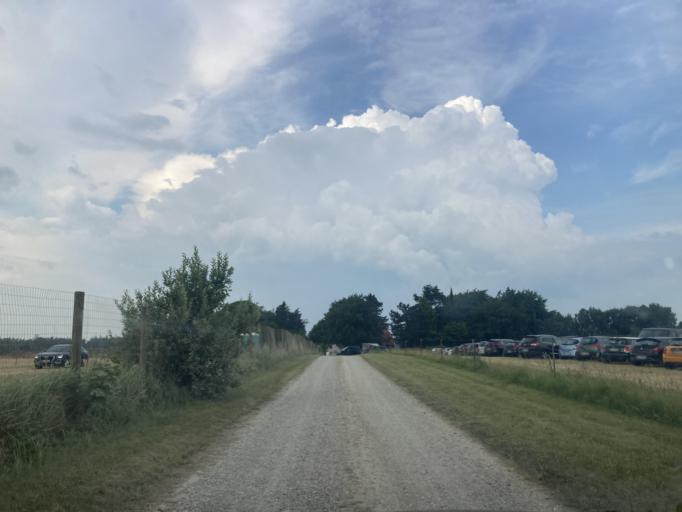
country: DK
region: Zealand
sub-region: Roskilde Kommune
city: Vindinge
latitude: 55.6131
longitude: 12.1046
